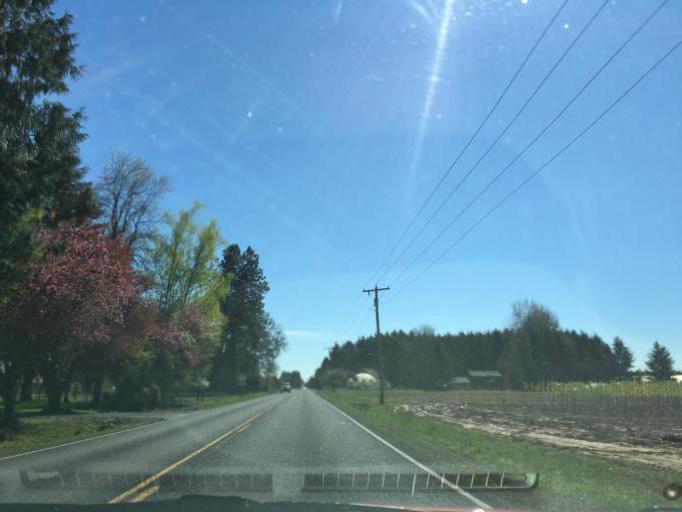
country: US
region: Oregon
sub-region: Clackamas County
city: Canby
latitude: 45.2207
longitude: -122.7228
